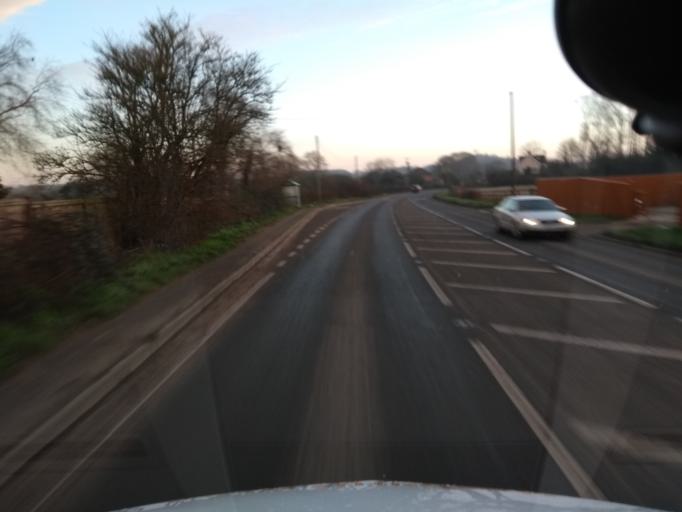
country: GB
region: England
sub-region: Somerset
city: Puriton
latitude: 51.1456
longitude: -2.9703
